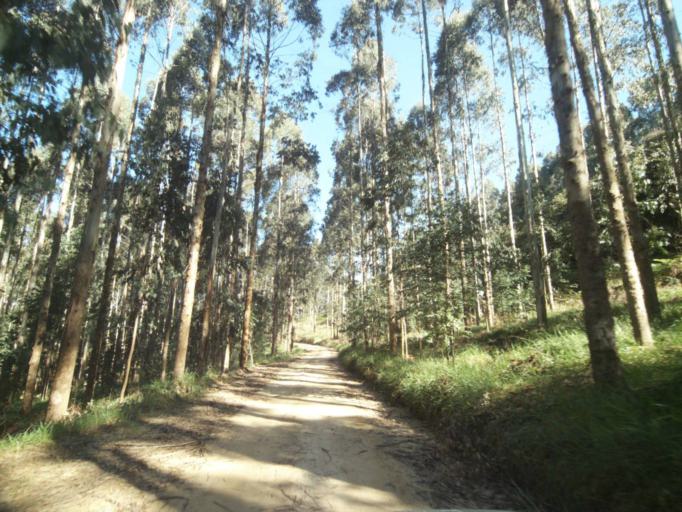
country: BR
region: Parana
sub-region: Tibagi
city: Tibagi
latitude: -24.5566
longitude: -50.4722
